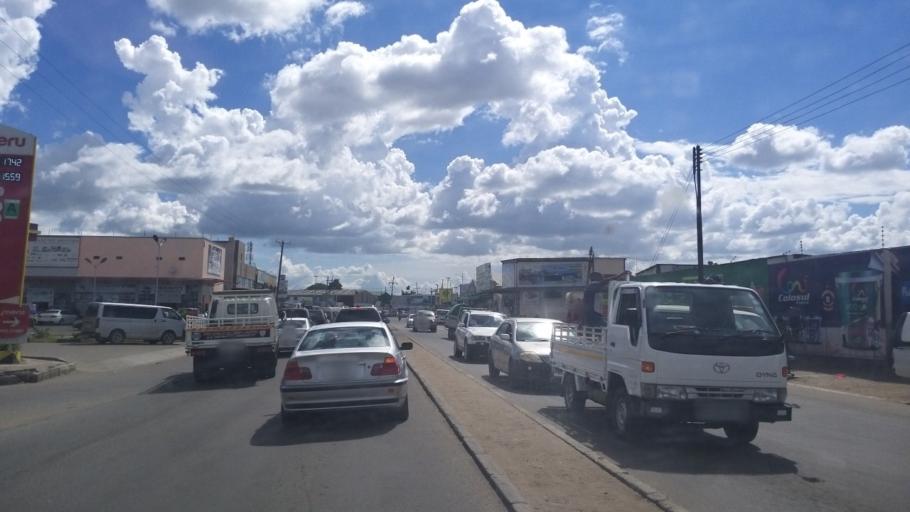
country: ZM
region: Lusaka
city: Lusaka
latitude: -15.4110
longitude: 28.2776
